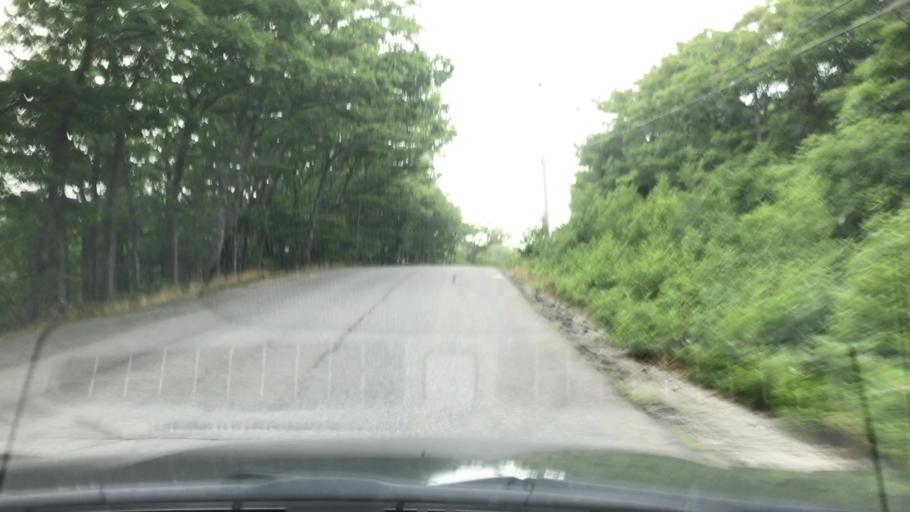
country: US
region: Maine
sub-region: Hancock County
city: Bar Harbor
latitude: 44.3527
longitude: -68.1838
